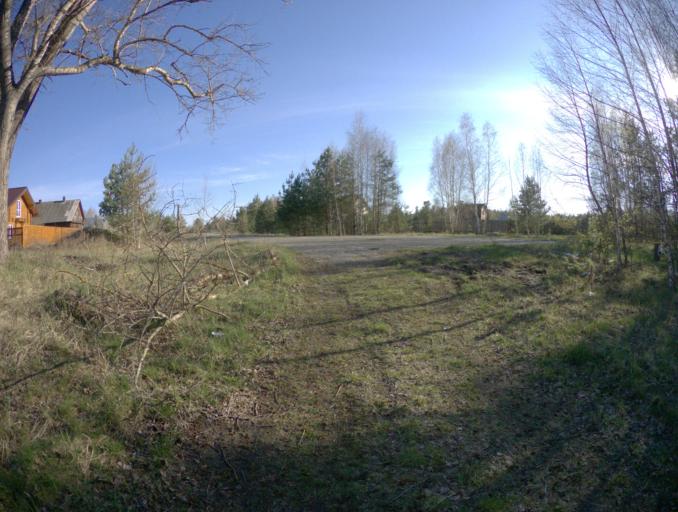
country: RU
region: Vladimir
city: Ivanishchi
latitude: 55.6665
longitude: 40.3880
